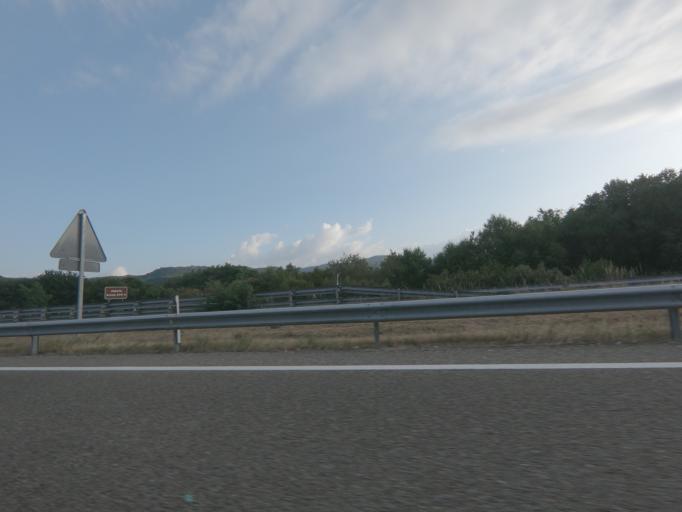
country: ES
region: Galicia
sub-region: Provincia de Ourense
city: Allariz
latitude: 42.1979
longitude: -7.7810
